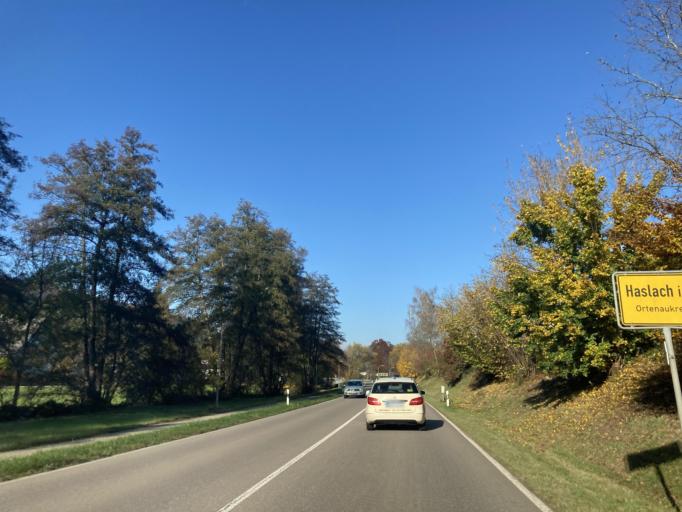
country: DE
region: Baden-Wuerttemberg
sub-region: Freiburg Region
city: Muhlenbach
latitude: 48.2701
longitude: 8.0935
